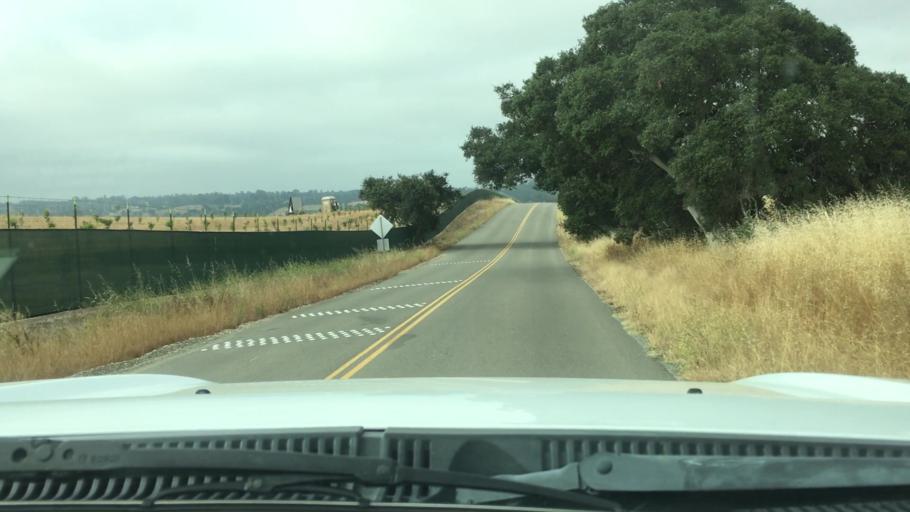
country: US
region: California
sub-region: San Luis Obispo County
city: Arroyo Grande
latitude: 35.1038
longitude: -120.5581
